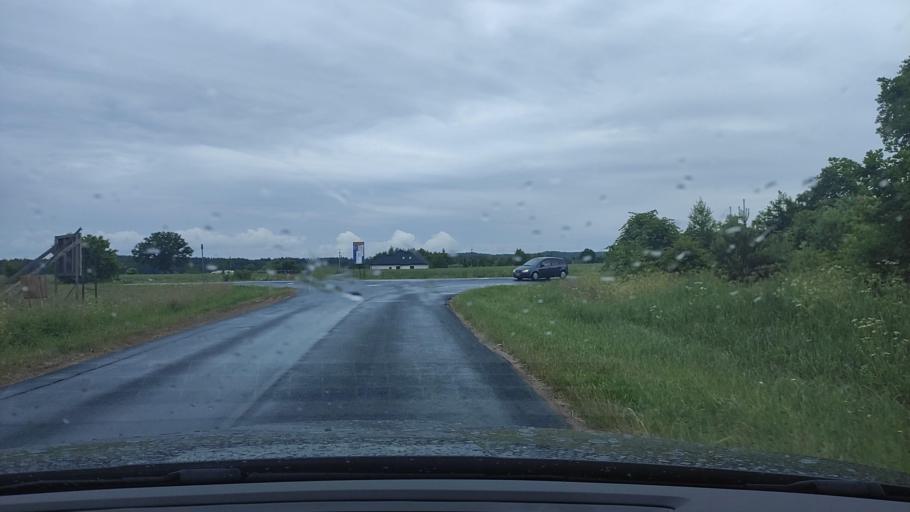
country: PL
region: West Pomeranian Voivodeship
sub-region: Powiat slawienski
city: Slawno
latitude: 54.5096
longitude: 16.5788
